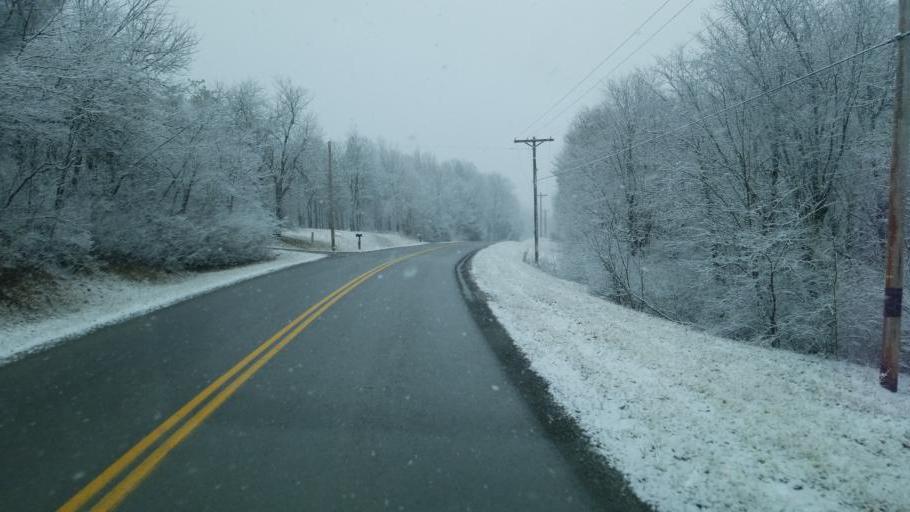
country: US
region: Ohio
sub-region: Logan County
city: Bellefontaine
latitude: 40.3395
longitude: -83.6488
